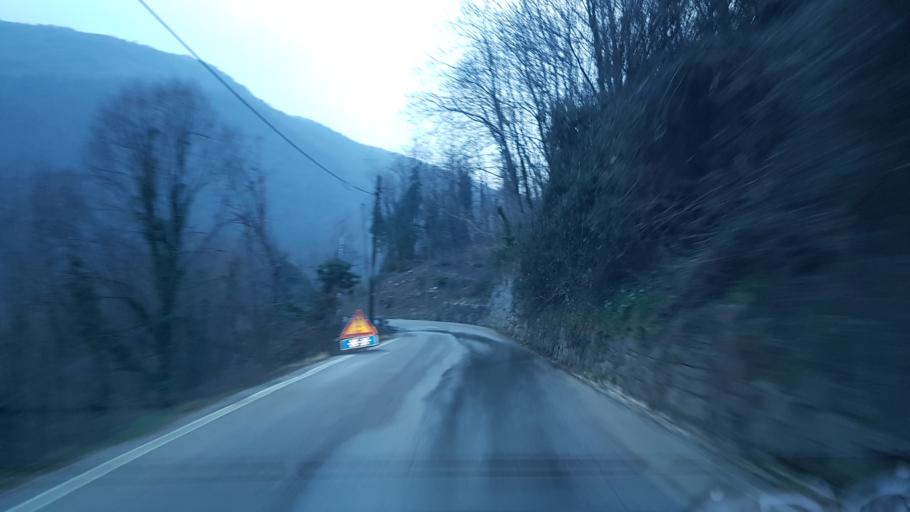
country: IT
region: Friuli Venezia Giulia
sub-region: Provincia di Udine
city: Attimis
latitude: 46.1963
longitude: 13.3388
